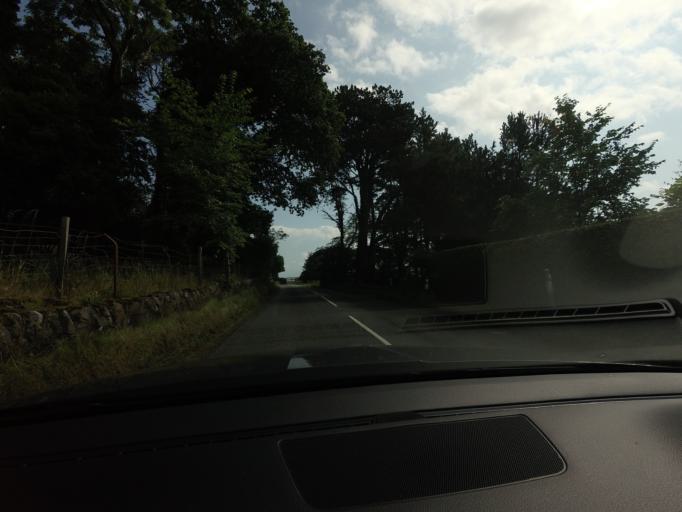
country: GB
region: Scotland
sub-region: Highland
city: Evanton
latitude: 57.6268
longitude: -4.3713
